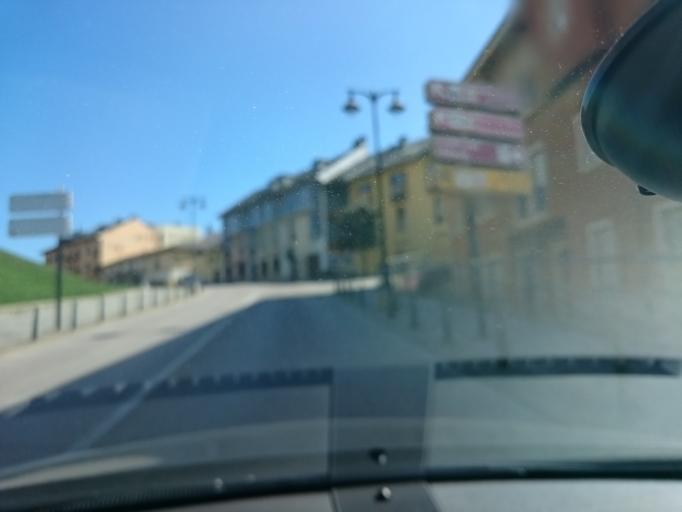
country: ES
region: Castille and Leon
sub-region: Provincia de Leon
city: Ponferrada
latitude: 42.5433
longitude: -6.5947
